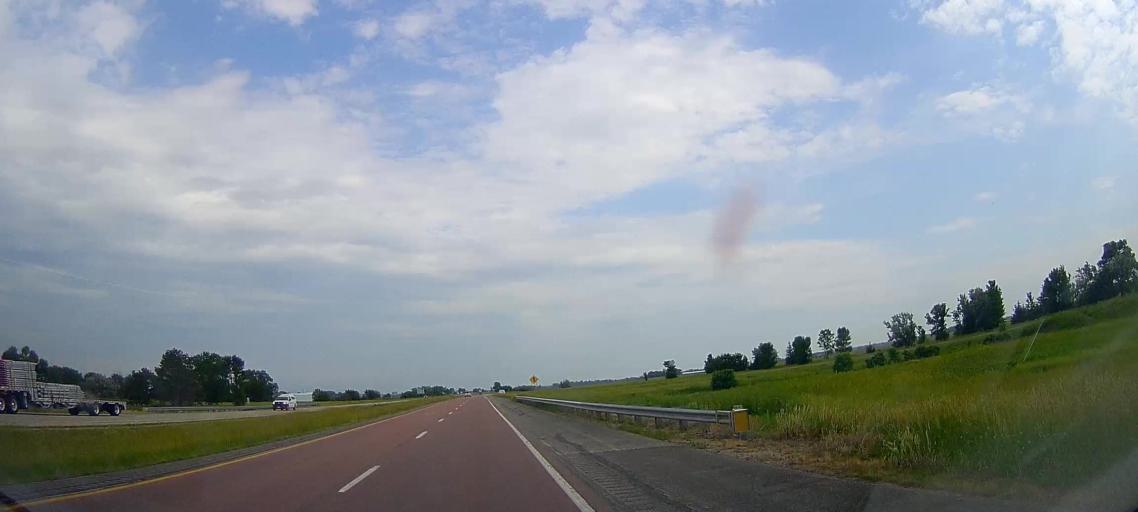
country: US
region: Iowa
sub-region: Monona County
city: Onawa
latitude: 42.0254
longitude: -96.1315
